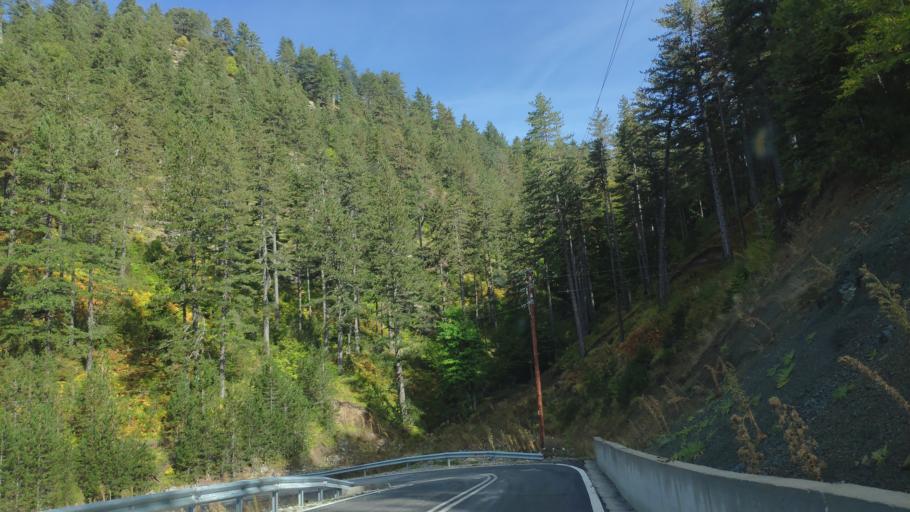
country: AL
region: Korce
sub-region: Rrethi i Devollit
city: Miras
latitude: 40.3989
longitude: 20.9015
